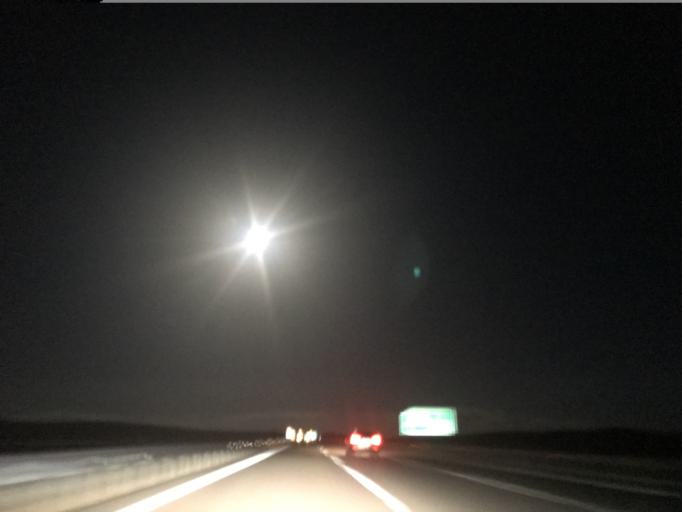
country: TR
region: Nigde
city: Ulukisla
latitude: 37.6364
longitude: 34.5000
